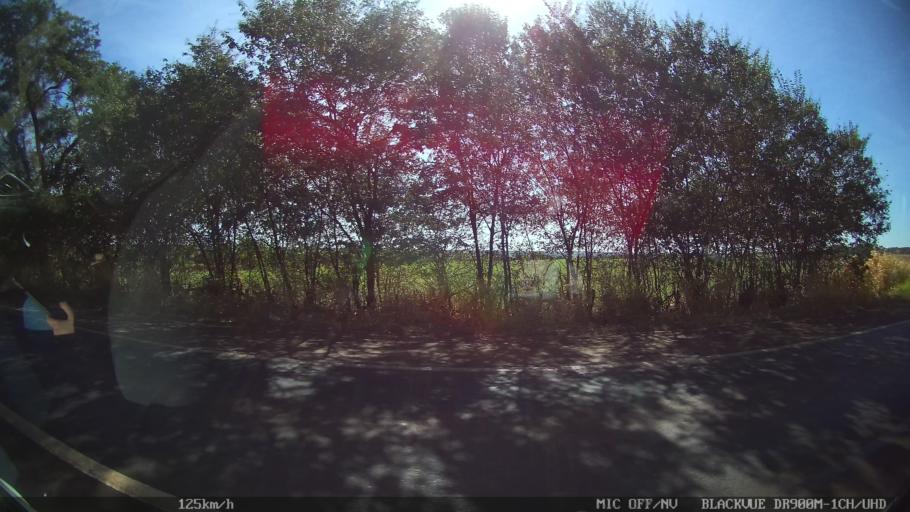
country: BR
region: Sao Paulo
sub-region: Barretos
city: Barretos
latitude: -20.5361
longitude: -48.6068
